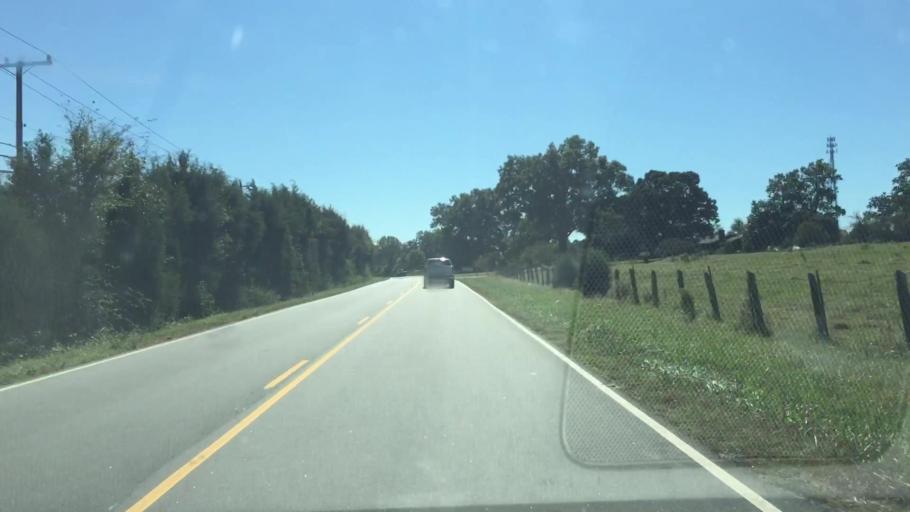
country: US
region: North Carolina
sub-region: Rowan County
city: Enochville
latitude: 35.4562
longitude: -80.7322
